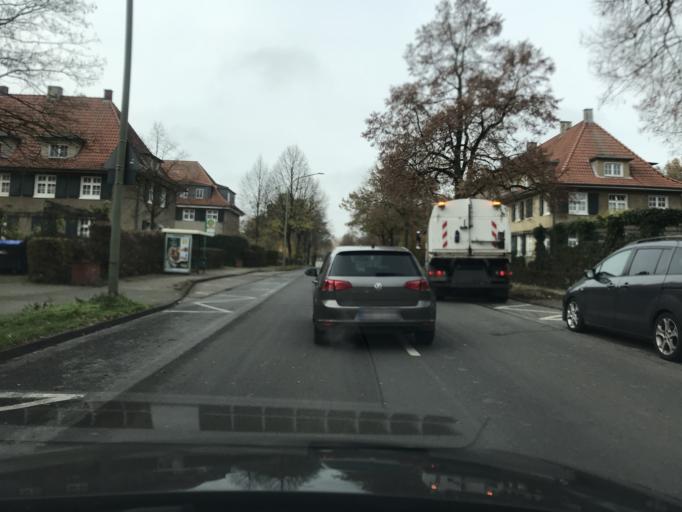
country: DE
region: North Rhine-Westphalia
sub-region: Regierungsbezirk Arnsberg
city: Hamm
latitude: 51.7070
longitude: 7.8104
